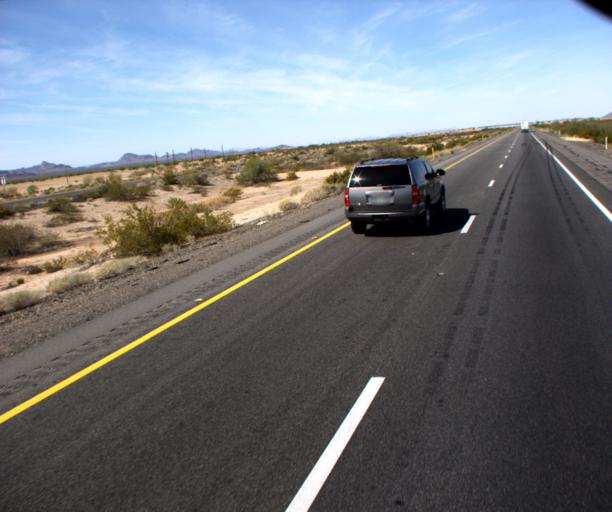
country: US
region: Arizona
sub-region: La Paz County
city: Salome
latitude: 33.5673
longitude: -113.3399
